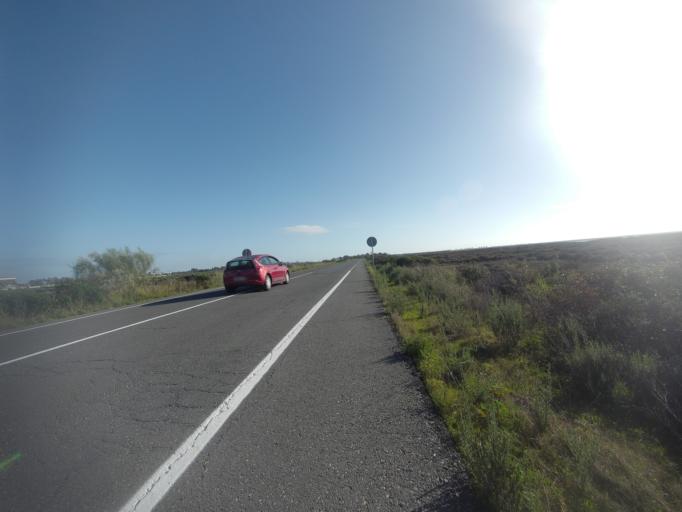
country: ES
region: Andalusia
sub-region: Provincia de Huelva
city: Huelva
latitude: 37.2482
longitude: -6.9672
